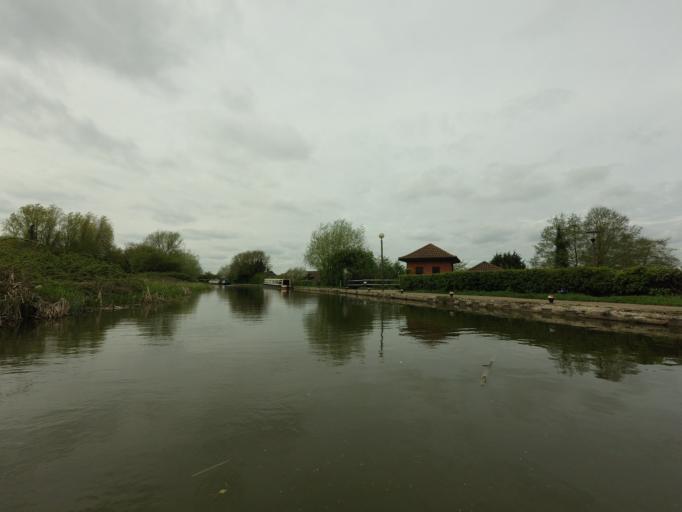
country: GB
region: England
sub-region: Milton Keynes
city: Newport Pagnell
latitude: 52.0733
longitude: -0.7467
